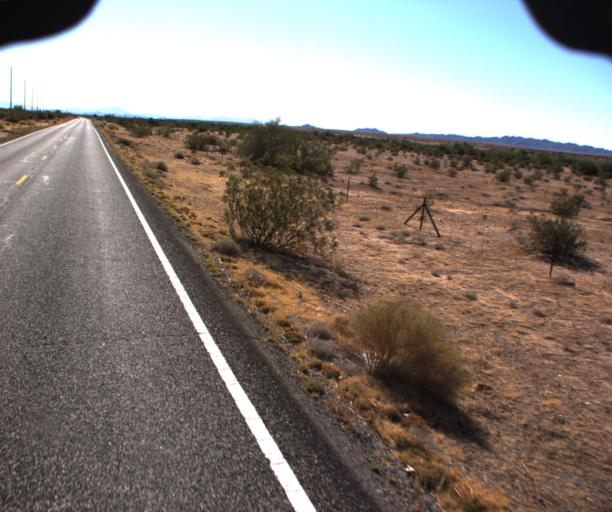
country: US
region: Arizona
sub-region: La Paz County
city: Parker
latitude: 33.9958
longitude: -114.1837
